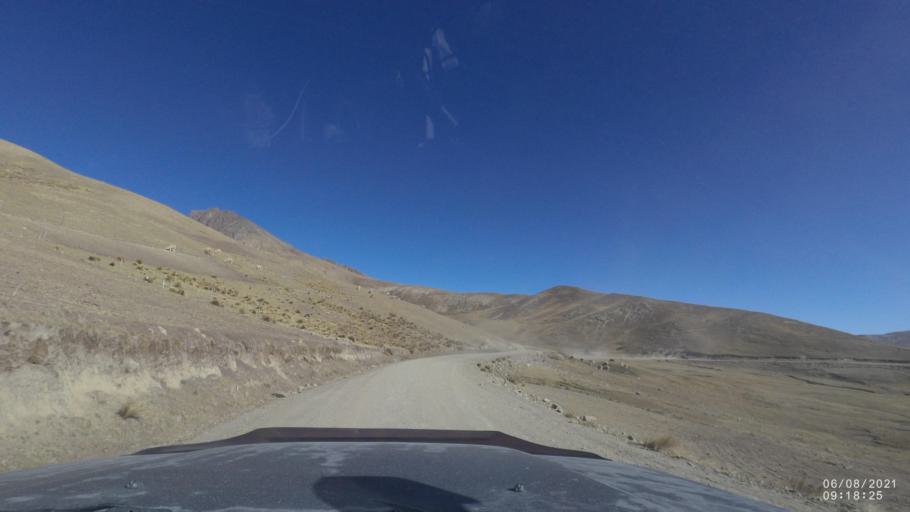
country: BO
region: Cochabamba
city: Colchani
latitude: -17.0348
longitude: -66.5304
